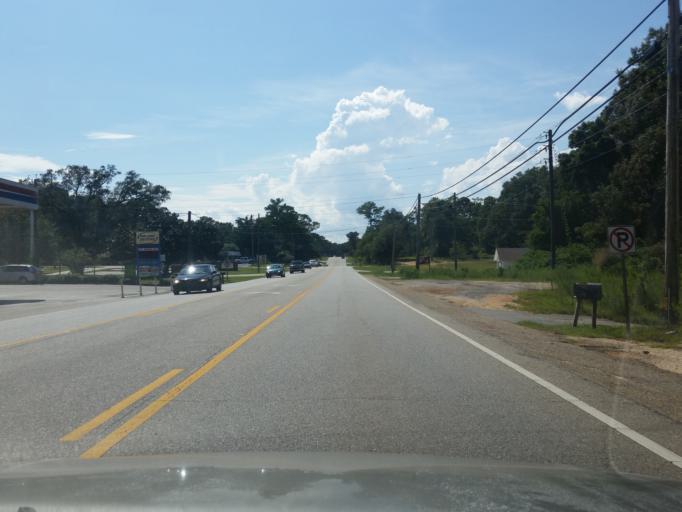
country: US
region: Alabama
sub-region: Baldwin County
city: Spanish Fort
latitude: 30.6720
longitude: -87.8823
